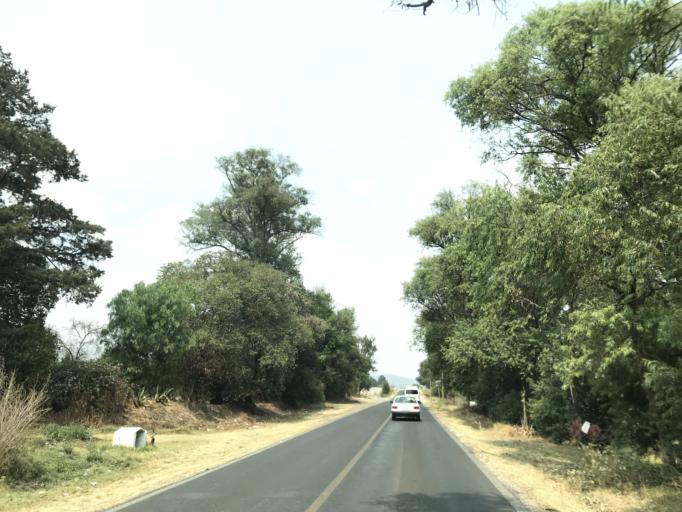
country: MX
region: Tlaxcala
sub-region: Ixtacuixtla de Mariano Matamoros
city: Santa Justina Ecatepec
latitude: 19.3162
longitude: -98.3229
